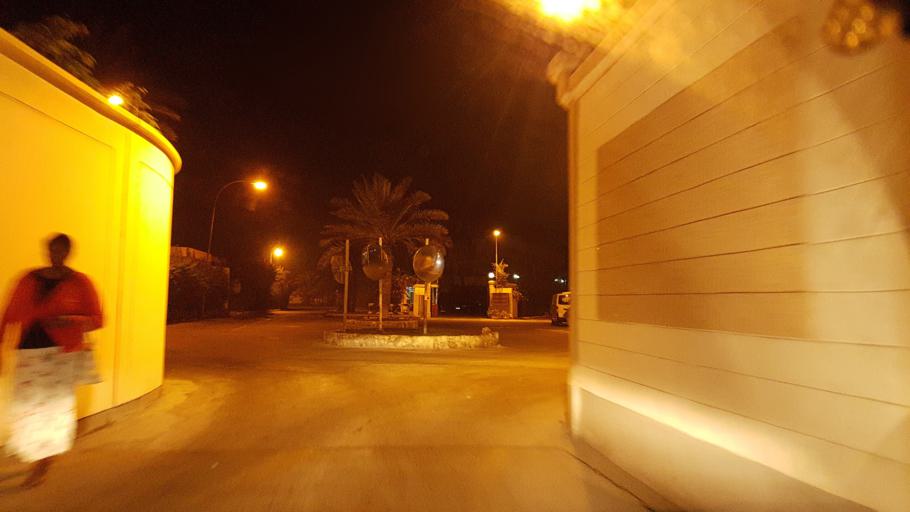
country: BH
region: Manama
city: Jidd Hafs
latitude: 26.2224
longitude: 50.4934
